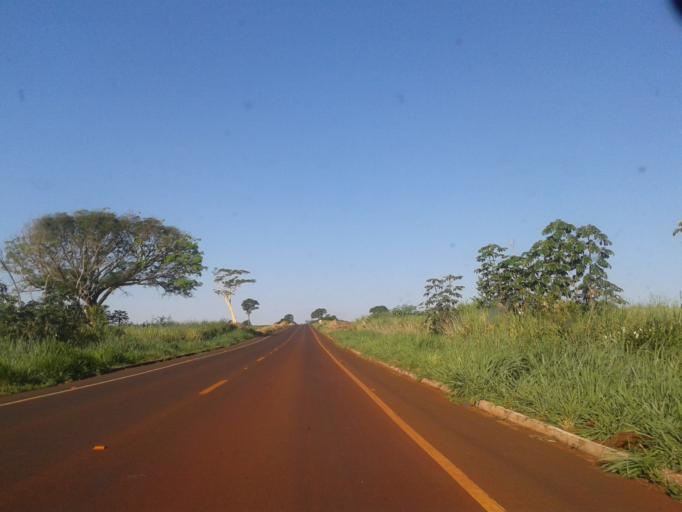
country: BR
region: Minas Gerais
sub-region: Capinopolis
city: Capinopolis
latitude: -18.7121
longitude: -49.7988
